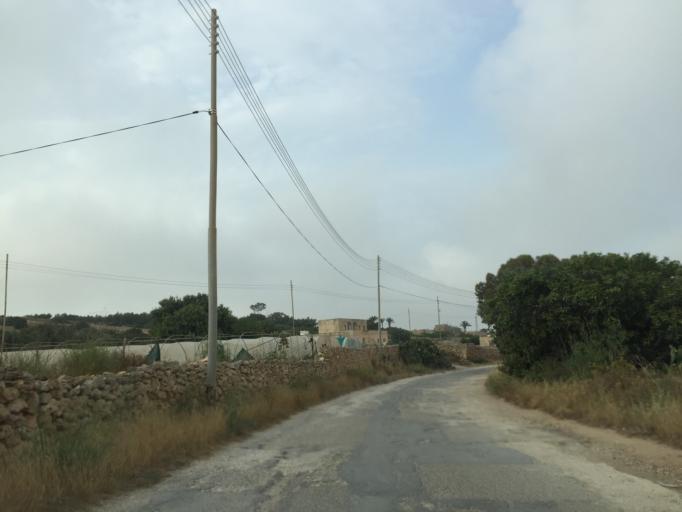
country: MT
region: L-Imgarr
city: Imgarr
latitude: 35.9337
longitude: 14.3878
